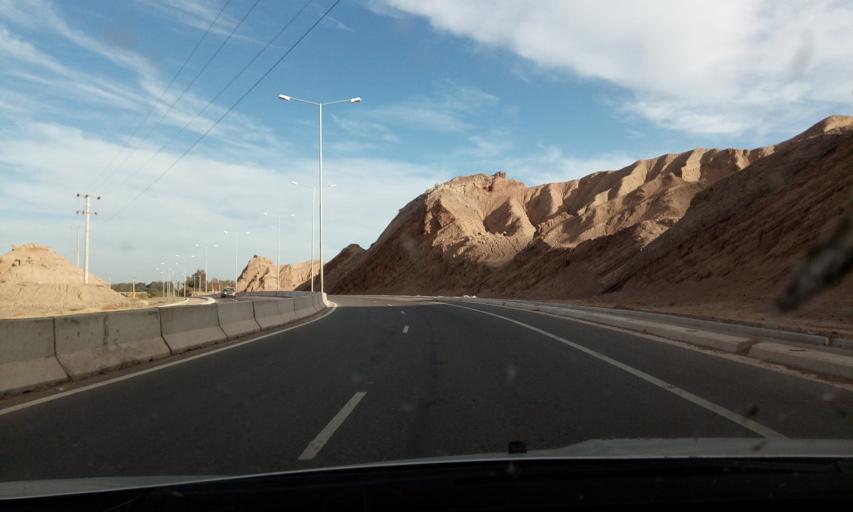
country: AR
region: San Juan
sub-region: Departamento de Rivadavia
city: Rivadavia
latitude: -31.4893
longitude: -68.6495
